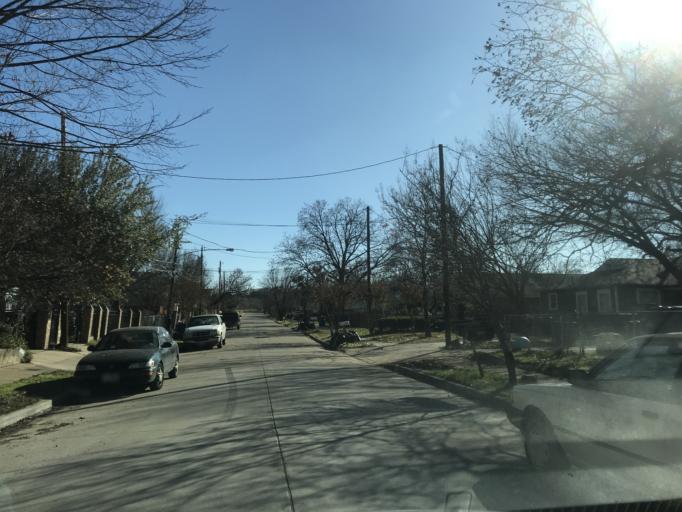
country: US
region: Texas
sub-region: Dallas County
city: Cockrell Hill
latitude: 32.7726
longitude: -96.9075
